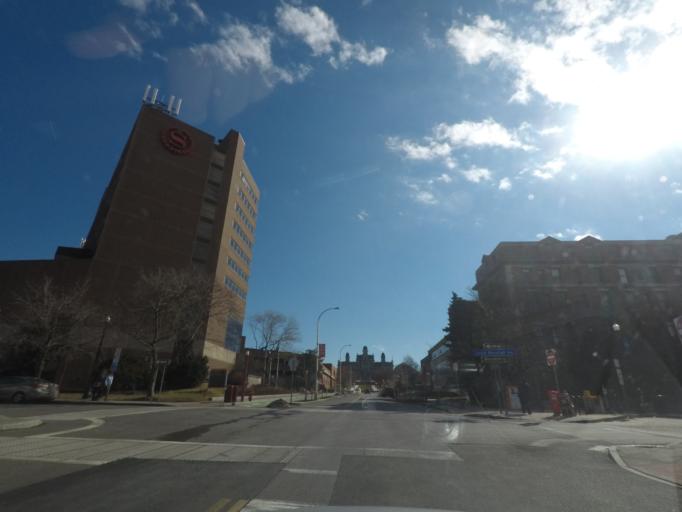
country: US
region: New York
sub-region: Onondaga County
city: Syracuse
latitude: 43.0418
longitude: -76.1345
